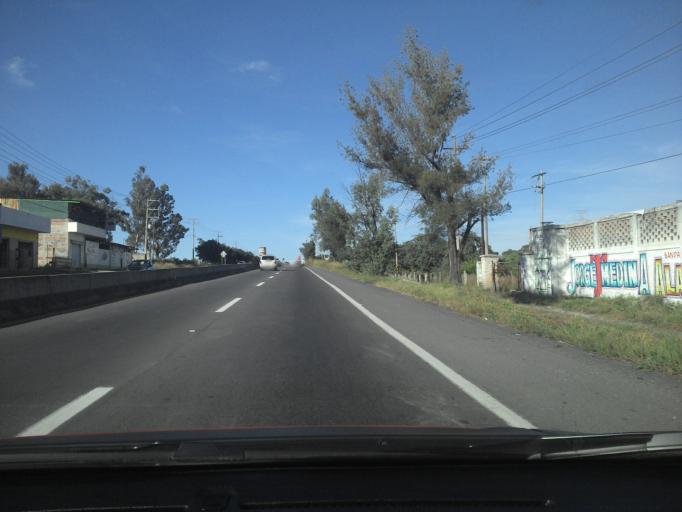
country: MX
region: Jalisco
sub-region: Tala
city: Los Ruisenores
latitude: 20.6978
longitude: -103.6896
